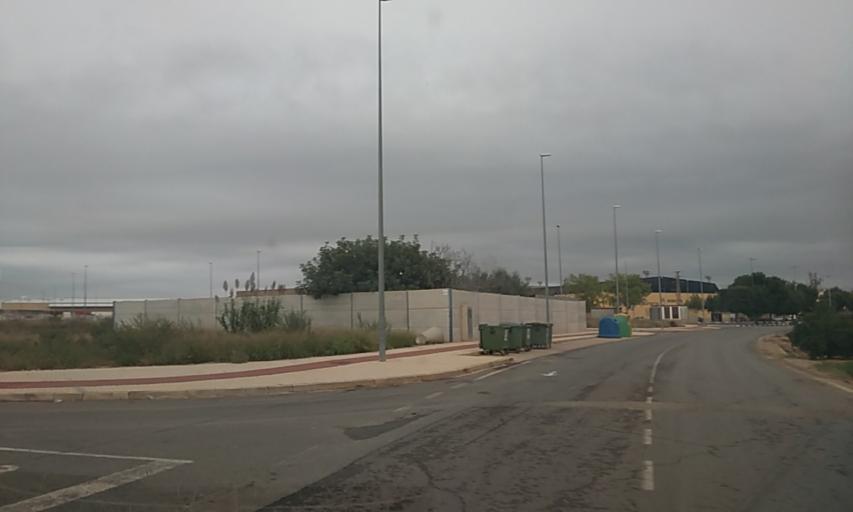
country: ES
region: Valencia
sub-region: Provincia de Valencia
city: L'Alcudia
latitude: 39.1909
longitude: -0.5174
